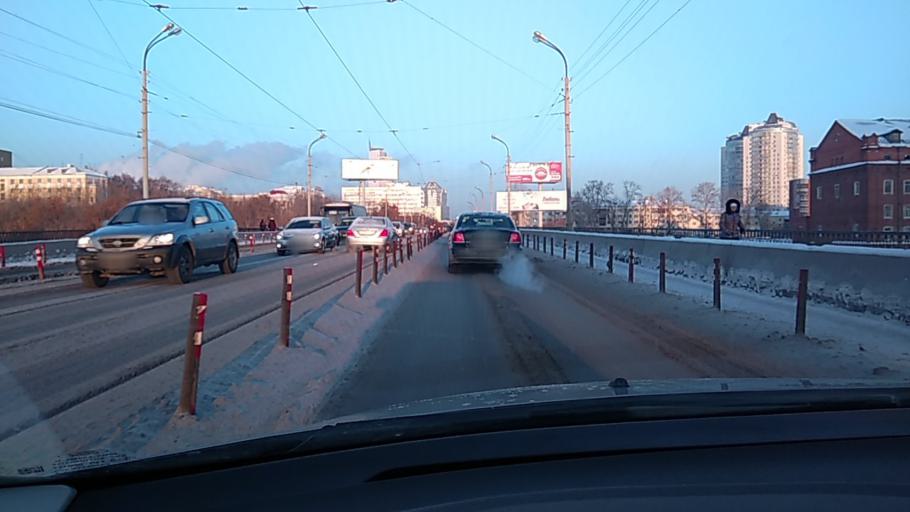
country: RU
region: Sverdlovsk
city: Yekaterinburg
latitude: 56.8476
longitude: 60.5893
